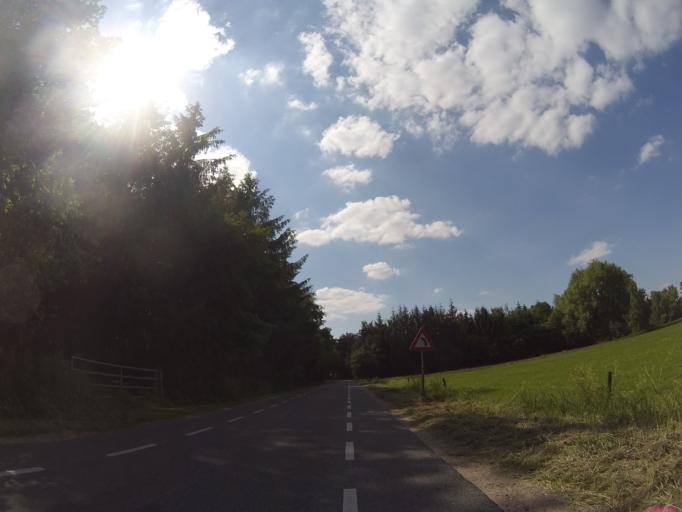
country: NL
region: Gelderland
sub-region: Gemeente Barneveld
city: Terschuur
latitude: 52.1585
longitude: 5.5072
